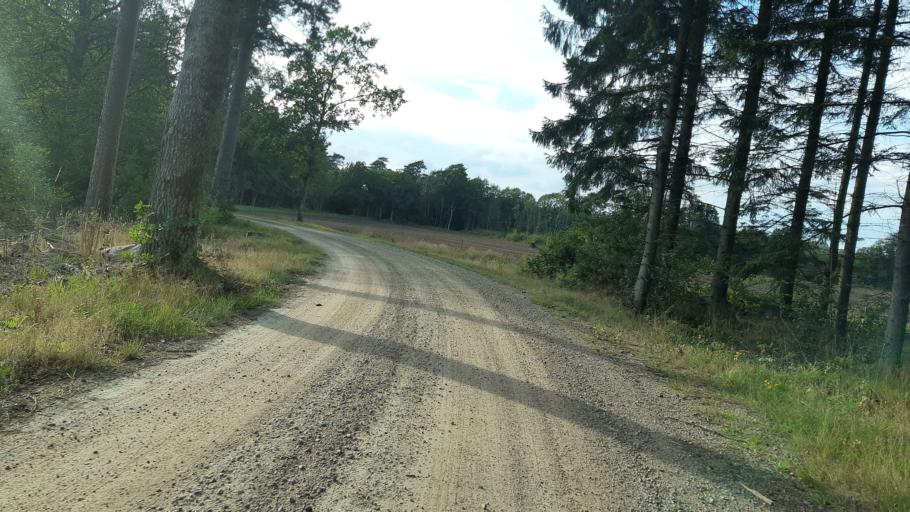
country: SE
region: Blekinge
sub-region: Ronneby Kommun
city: Kallinge
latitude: 56.2276
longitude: 15.3758
